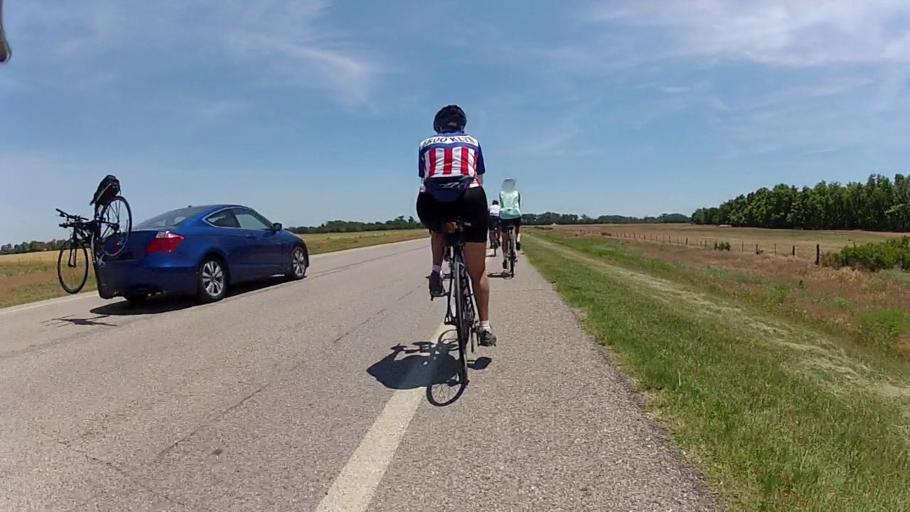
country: US
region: Kansas
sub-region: Barber County
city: Medicine Lodge
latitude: 37.2534
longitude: -98.4644
